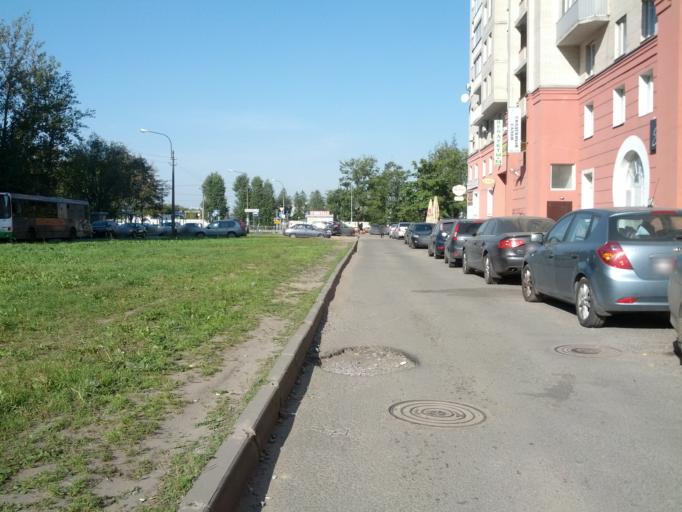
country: RU
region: St.-Petersburg
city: Kupchino
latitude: 59.8414
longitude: 30.3492
